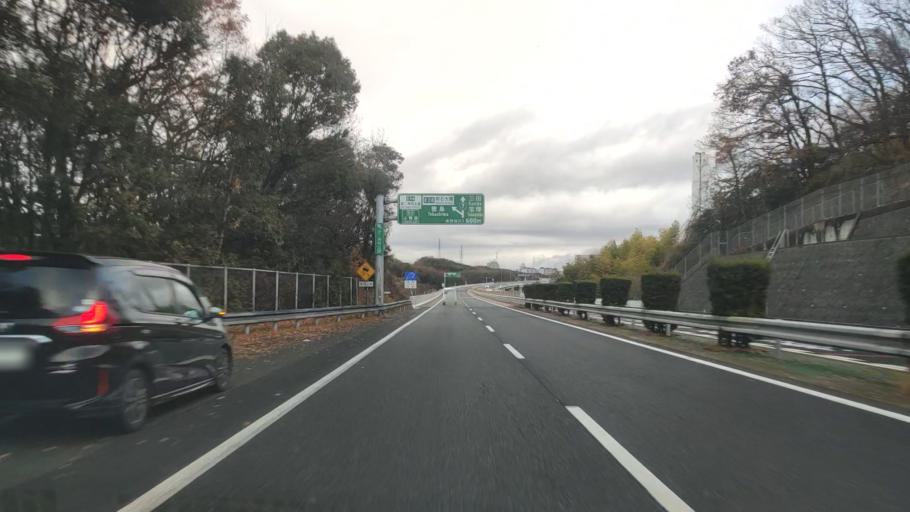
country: JP
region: Hyogo
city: Akashi
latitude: 34.6788
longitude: 135.0167
